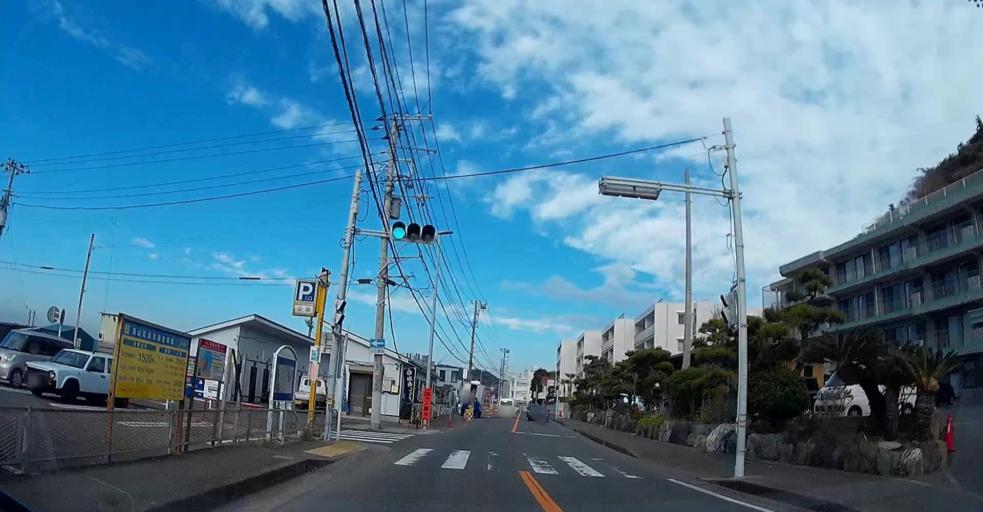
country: JP
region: Kanagawa
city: Hayama
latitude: 35.2683
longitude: 139.5703
